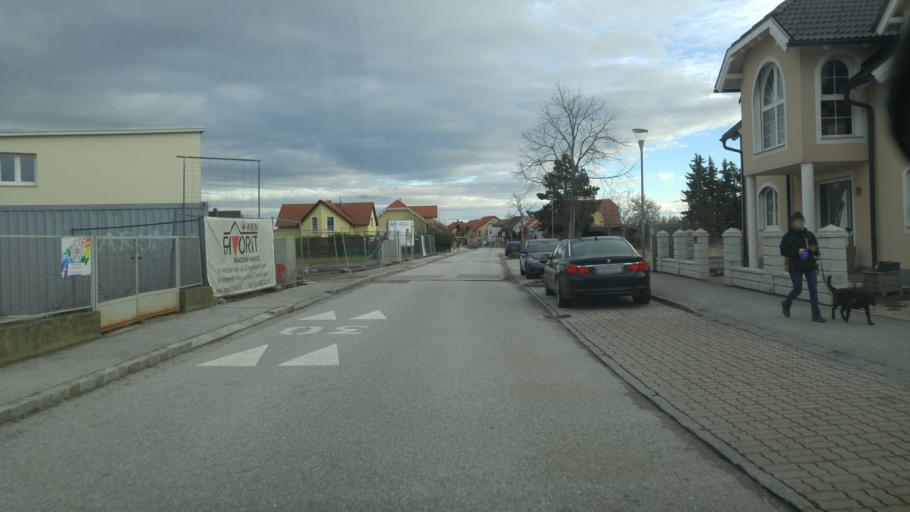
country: AT
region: Lower Austria
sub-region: Politischer Bezirk Baden
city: Bad Voslau
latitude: 47.9587
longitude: 16.2097
